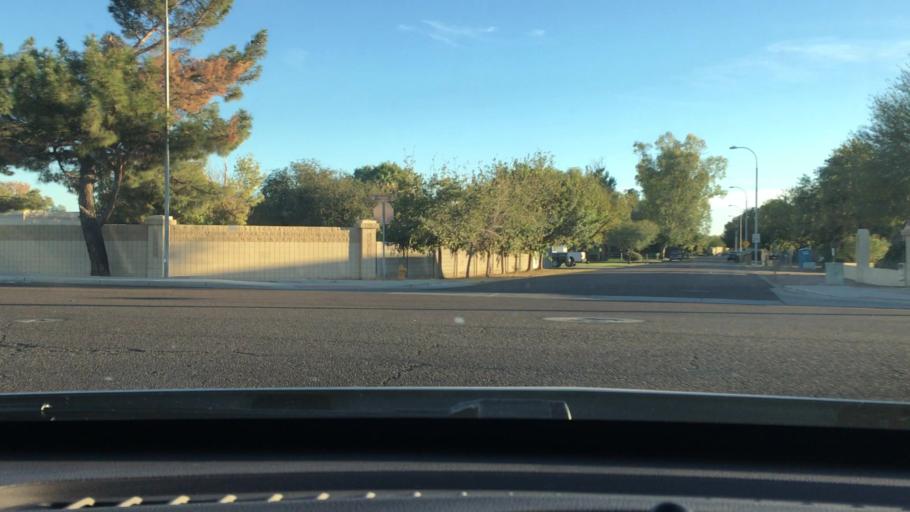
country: US
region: Arizona
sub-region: Maricopa County
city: Chandler
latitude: 33.2919
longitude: -111.8149
